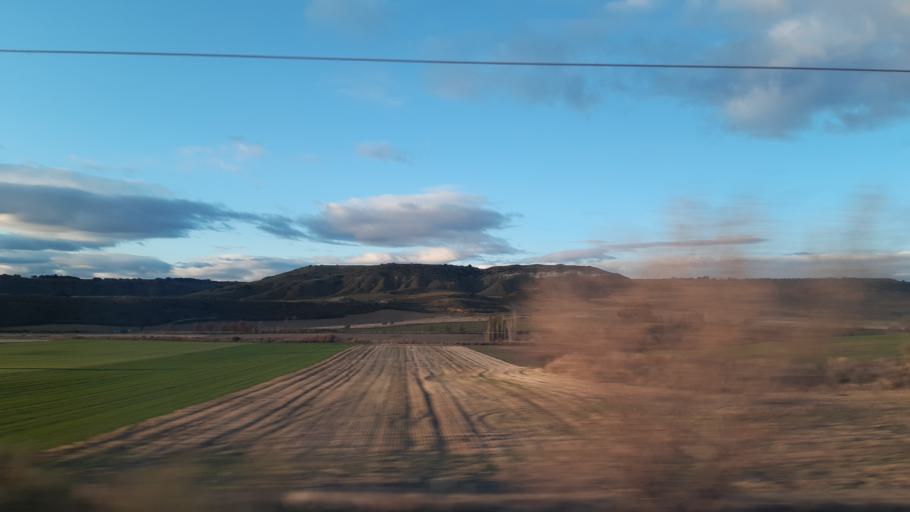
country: ES
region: Madrid
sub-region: Provincia de Madrid
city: Anchuelo
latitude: 40.4650
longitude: -3.2909
